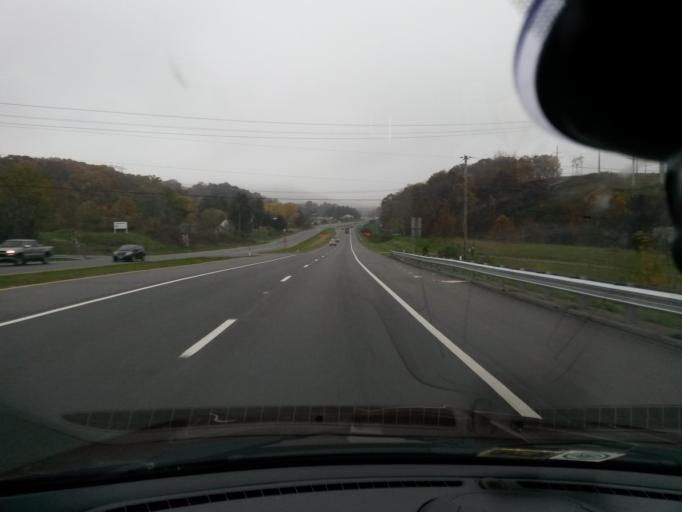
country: US
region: Virginia
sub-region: Botetourt County
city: Cloverdale
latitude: 37.3832
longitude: -79.8953
